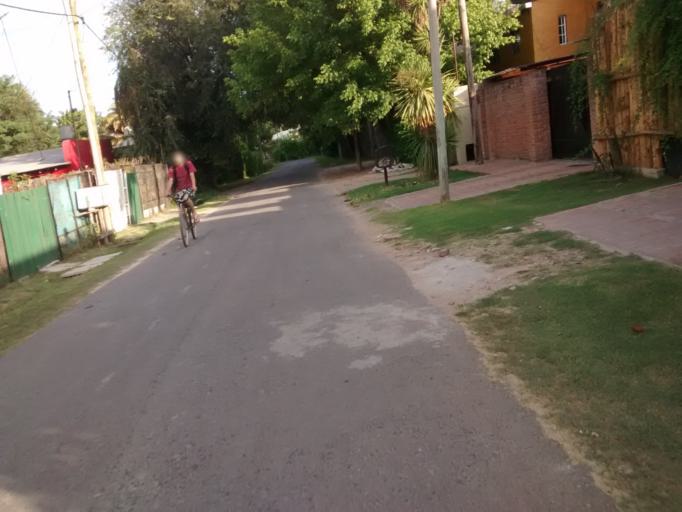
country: AR
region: Buenos Aires
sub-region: Partido de La Plata
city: La Plata
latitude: -34.8745
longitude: -58.0917
